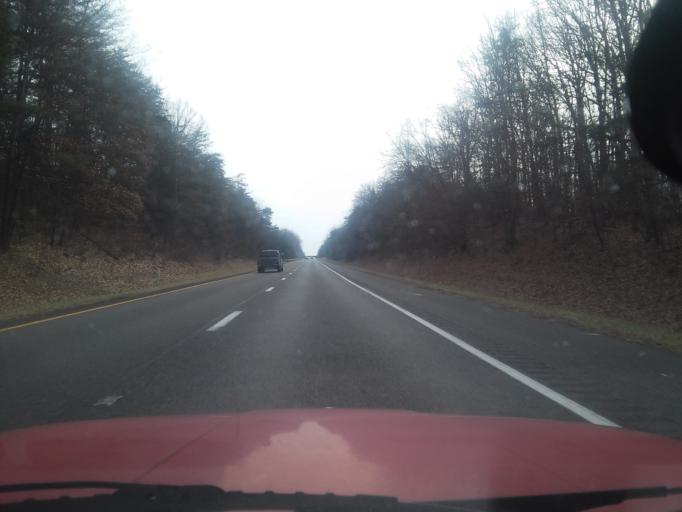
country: US
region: Virginia
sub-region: Louisa County
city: Louisa
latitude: 37.8512
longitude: -77.9901
